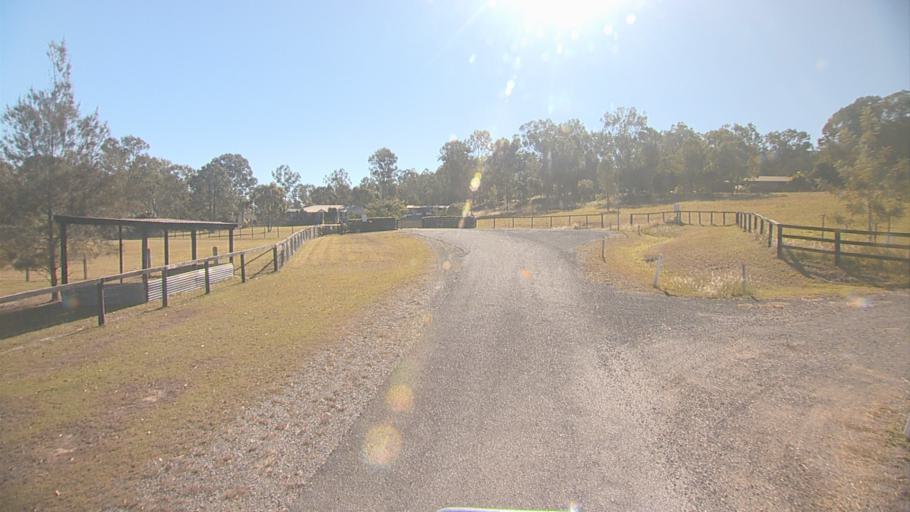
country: AU
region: Queensland
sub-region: Logan
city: Windaroo
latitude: -27.7794
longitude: 153.1442
